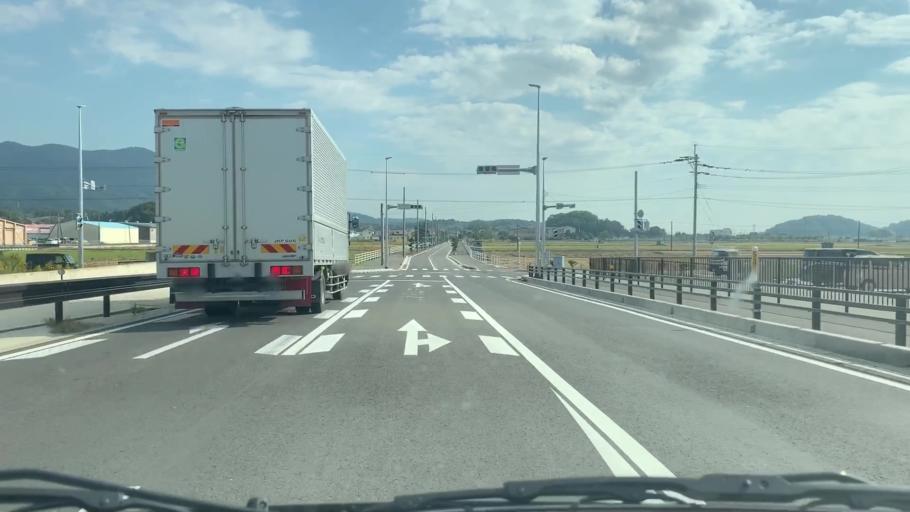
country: JP
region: Saga Prefecture
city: Takeocho-takeo
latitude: 33.2181
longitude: 130.0609
